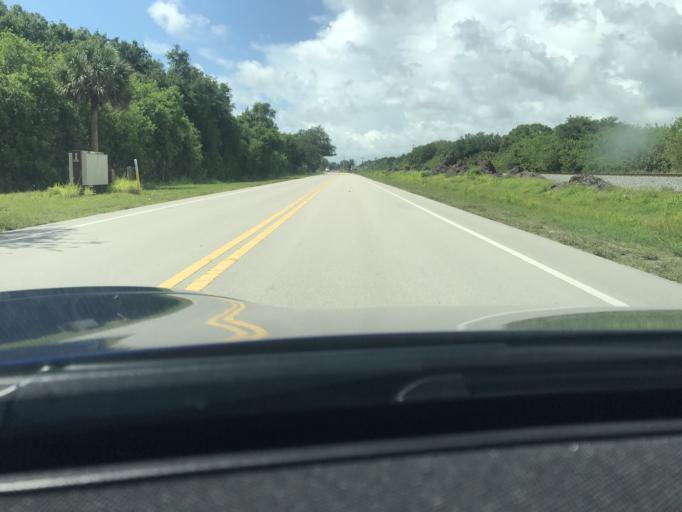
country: US
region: Florida
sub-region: Indian River County
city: Winter Beach
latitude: 27.7224
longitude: -80.4237
